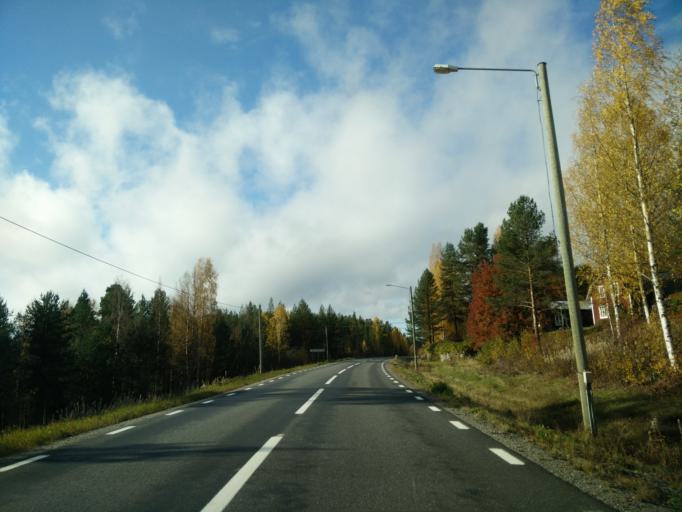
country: SE
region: Jaemtland
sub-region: Braecke Kommun
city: Braecke
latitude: 62.3913
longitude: 15.0736
